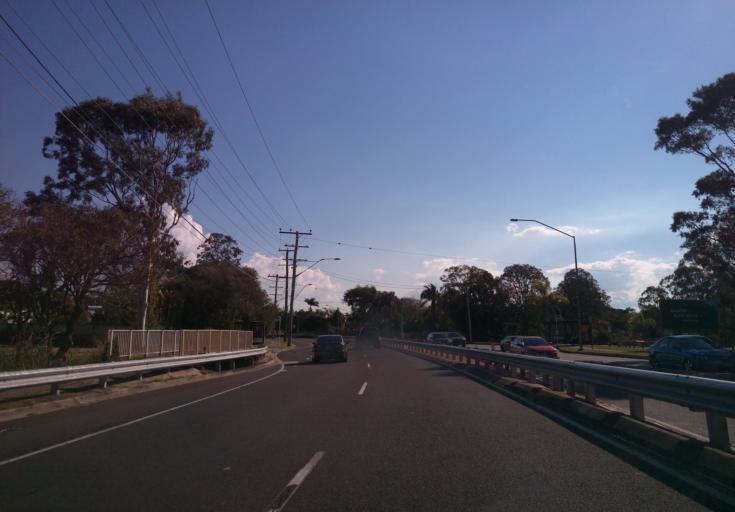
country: AU
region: Queensland
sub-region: Redland
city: Cleveland
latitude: -27.5214
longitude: 153.2112
